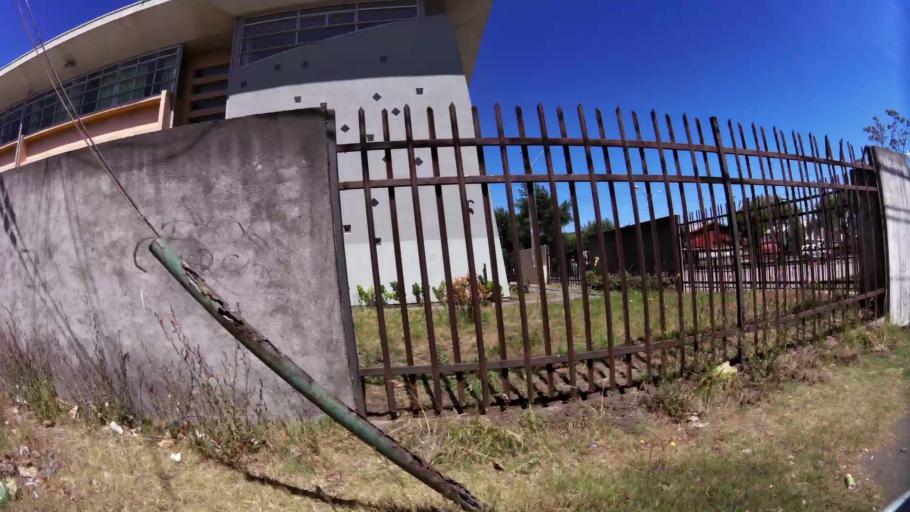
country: CL
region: Biobio
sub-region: Provincia de Concepcion
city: Talcahuano
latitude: -36.7599
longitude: -73.0940
